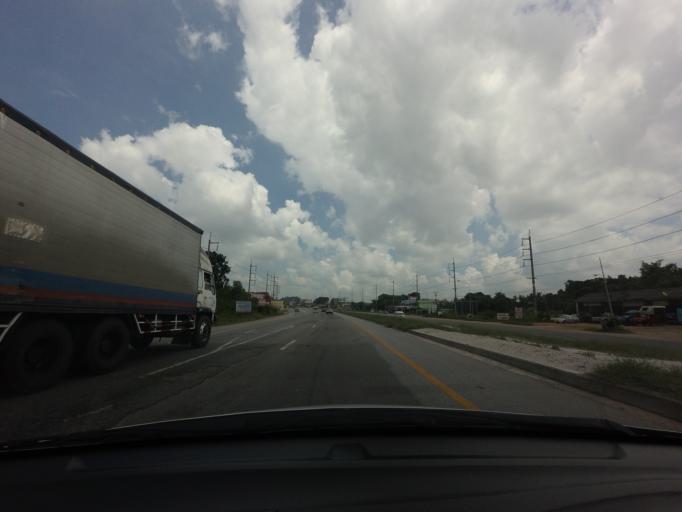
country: TH
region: Chachoengsao
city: Sanam Chai Khet
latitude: 13.7626
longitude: 101.5143
